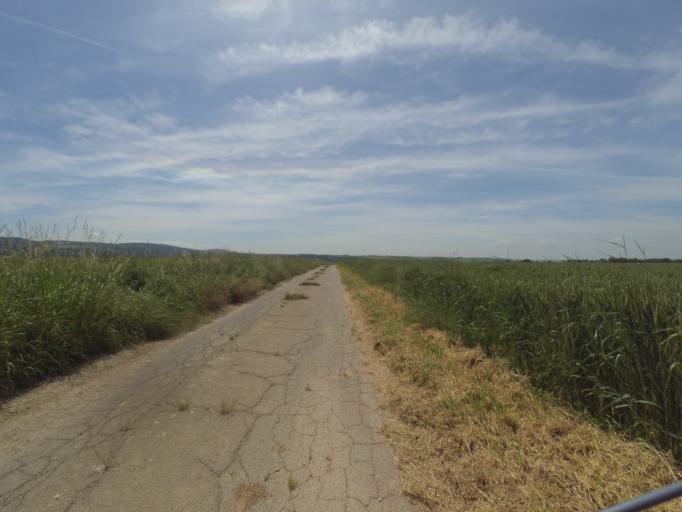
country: DE
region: Rheinland-Pfalz
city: Kobern-Gondorf
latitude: 50.3052
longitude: 7.4454
